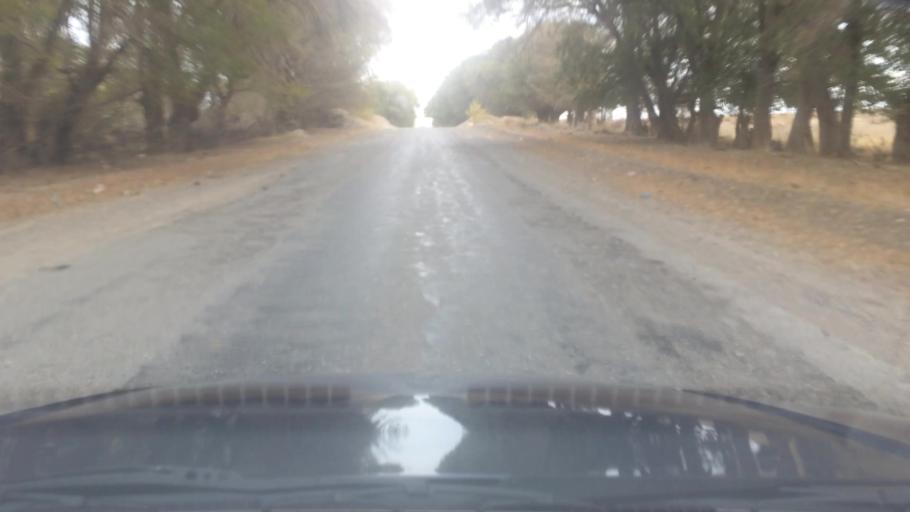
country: KG
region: Ysyk-Koel
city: Balykchy
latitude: 42.3029
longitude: 76.4797
